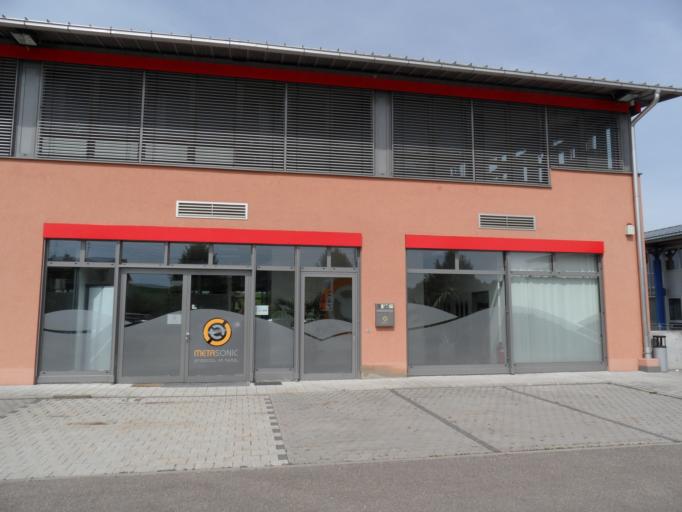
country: DE
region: Bavaria
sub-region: Upper Bavaria
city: Pfaffenhofen an der Ilm
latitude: 48.5186
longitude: 11.5102
